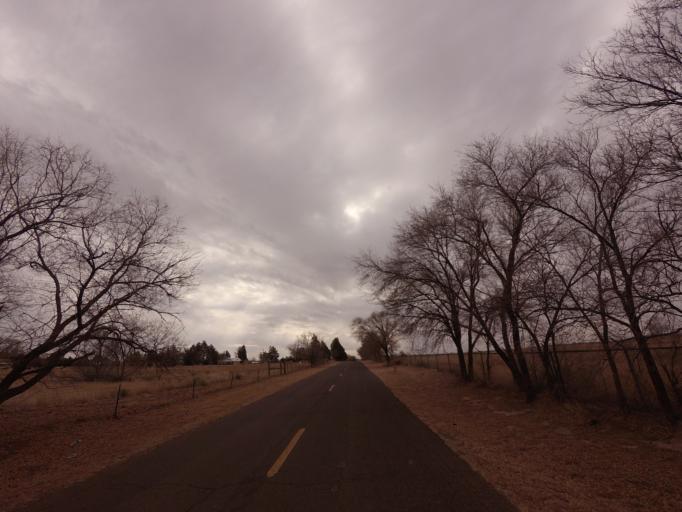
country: US
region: New Mexico
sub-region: Curry County
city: Clovis
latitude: 34.3789
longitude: -103.2053
